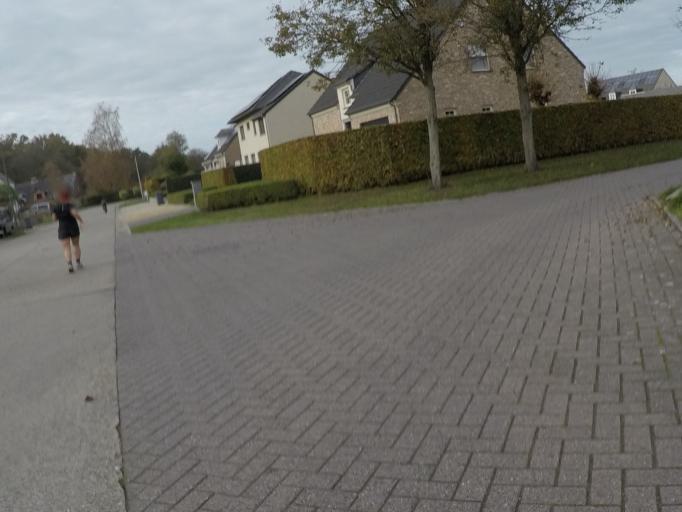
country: BE
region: Flanders
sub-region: Provincie Antwerpen
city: Nijlen
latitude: 51.1563
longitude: 4.6533
